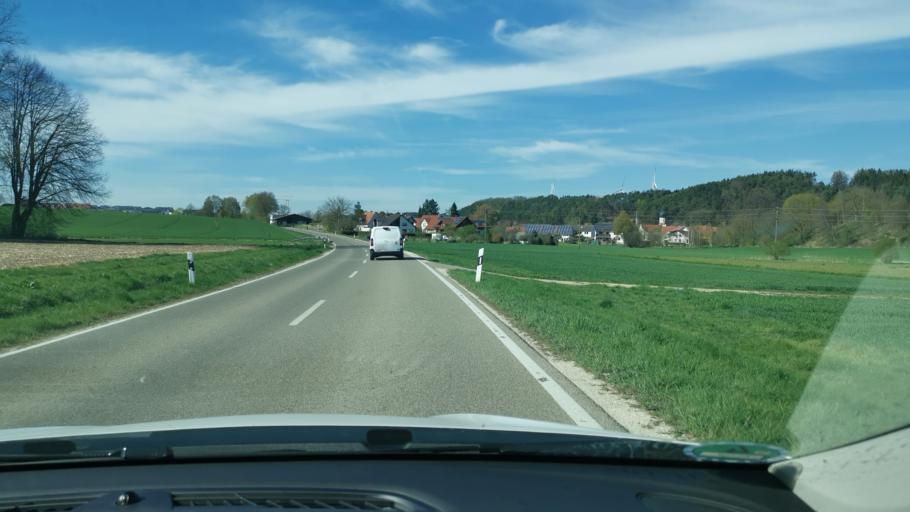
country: DE
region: Bavaria
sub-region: Swabia
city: Holzheim
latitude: 48.5800
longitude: 10.9652
